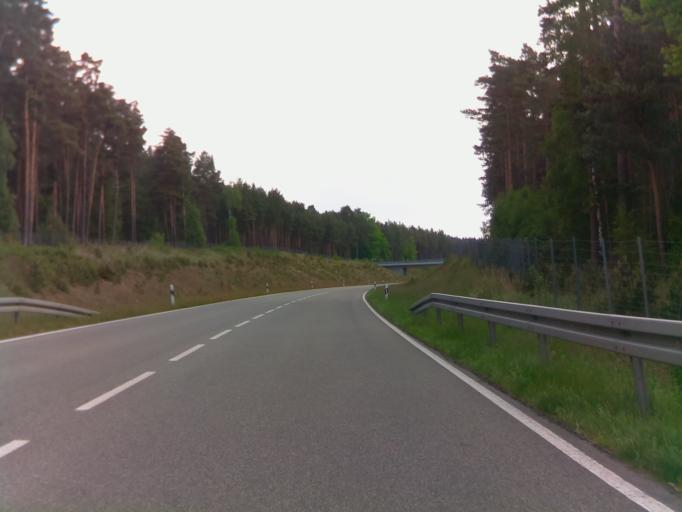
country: DE
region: Saxony-Anhalt
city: Uchtspringe
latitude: 52.5427
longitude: 11.5861
